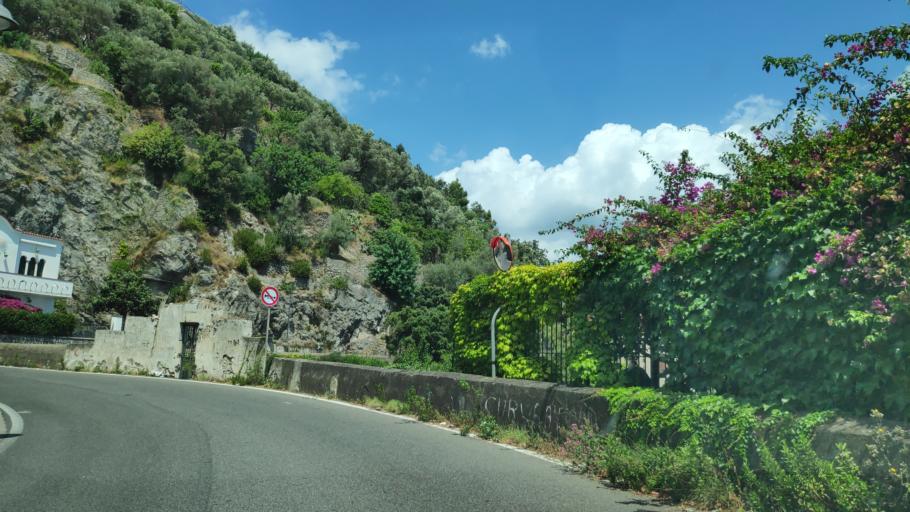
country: IT
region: Campania
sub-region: Provincia di Salerno
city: Atrani
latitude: 40.6415
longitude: 14.6163
